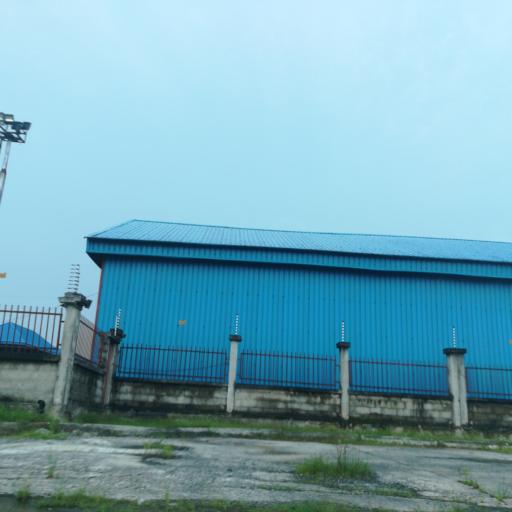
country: NG
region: Rivers
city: Port Harcourt
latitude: 4.7482
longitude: 7.0051
